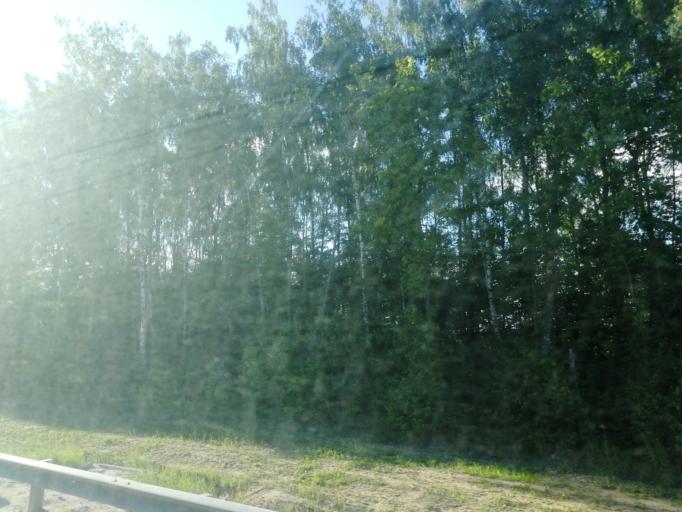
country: RU
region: Tula
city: Novogurovskiy
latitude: 54.2794
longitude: 37.2252
